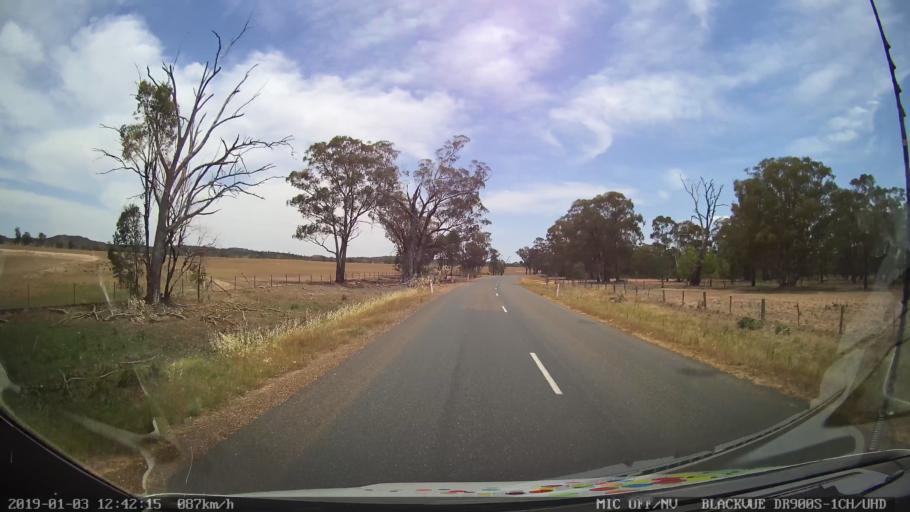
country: AU
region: New South Wales
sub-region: Weddin
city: Grenfell
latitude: -33.7895
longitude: 148.2121
